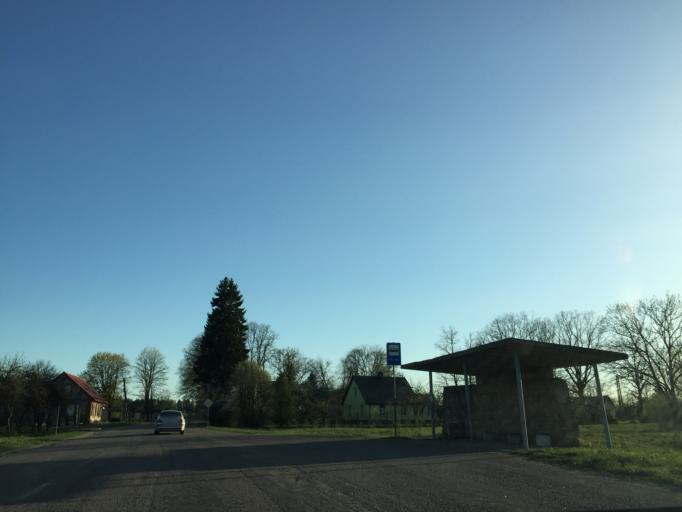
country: LV
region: Koknese
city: Koknese
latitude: 56.6777
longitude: 25.4817
